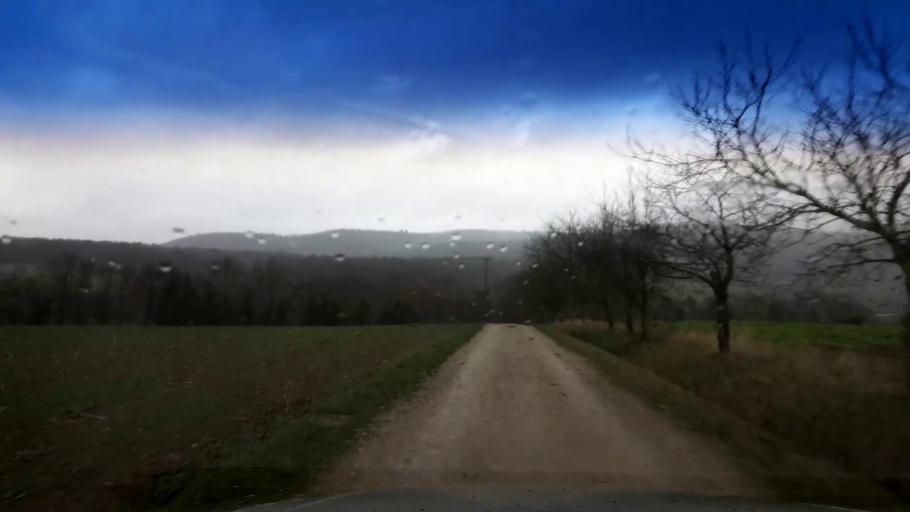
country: DE
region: Bavaria
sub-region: Upper Franconia
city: Litzendorf
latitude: 49.8665
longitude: 11.0316
